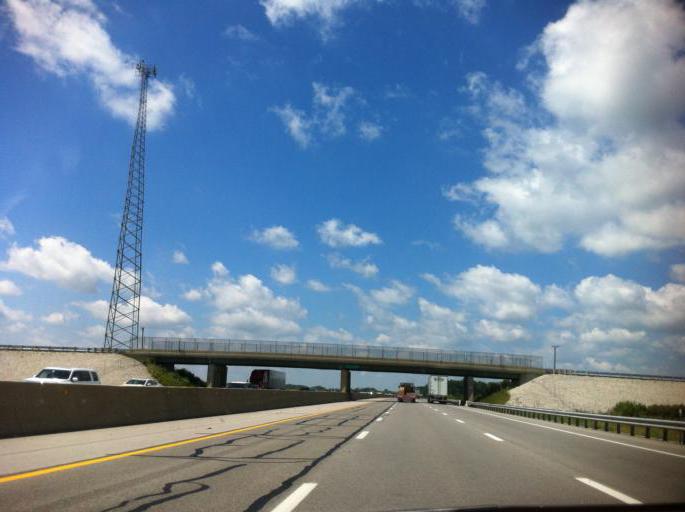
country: US
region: Ohio
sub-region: Sandusky County
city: Fremont
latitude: 41.3889
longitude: -83.0541
